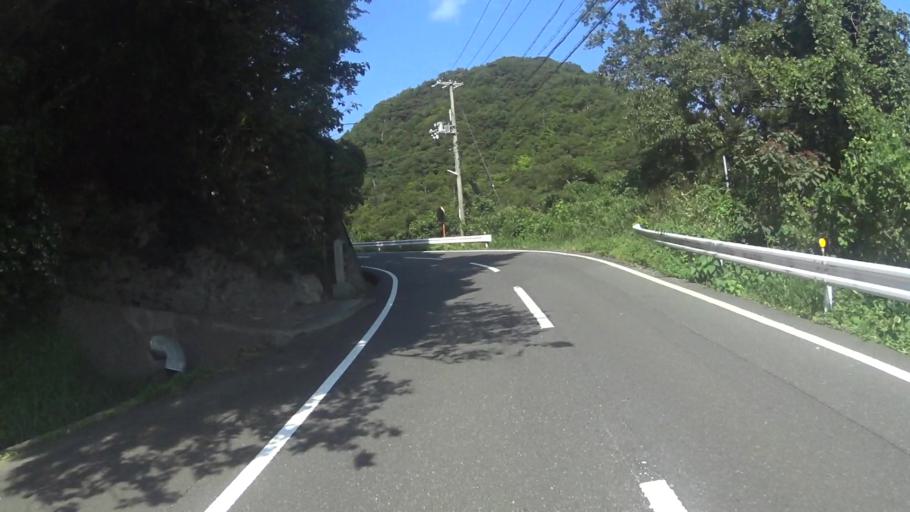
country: JP
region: Kyoto
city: Miyazu
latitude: 35.7040
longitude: 135.2823
